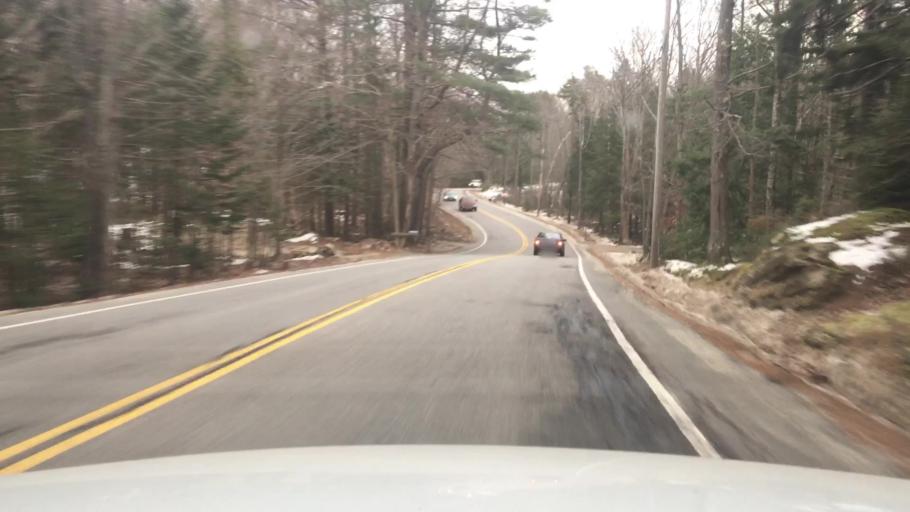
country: US
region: Maine
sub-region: Cumberland County
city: Freeport
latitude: 43.8781
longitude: -70.0469
